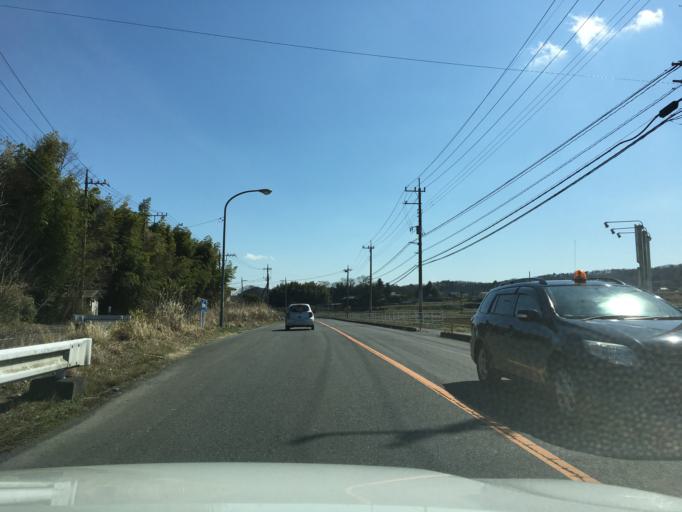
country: JP
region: Tochigi
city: Karasuyama
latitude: 36.7276
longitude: 140.1422
